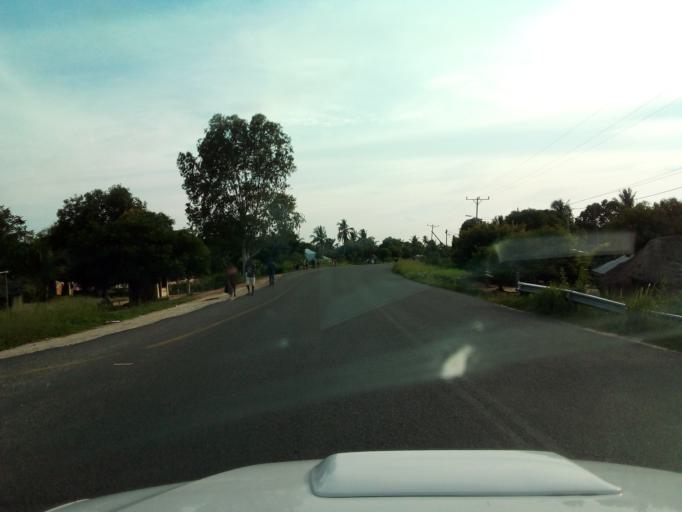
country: MZ
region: Zambezia
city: Quelimane
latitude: -17.4888
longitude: 37.0295
